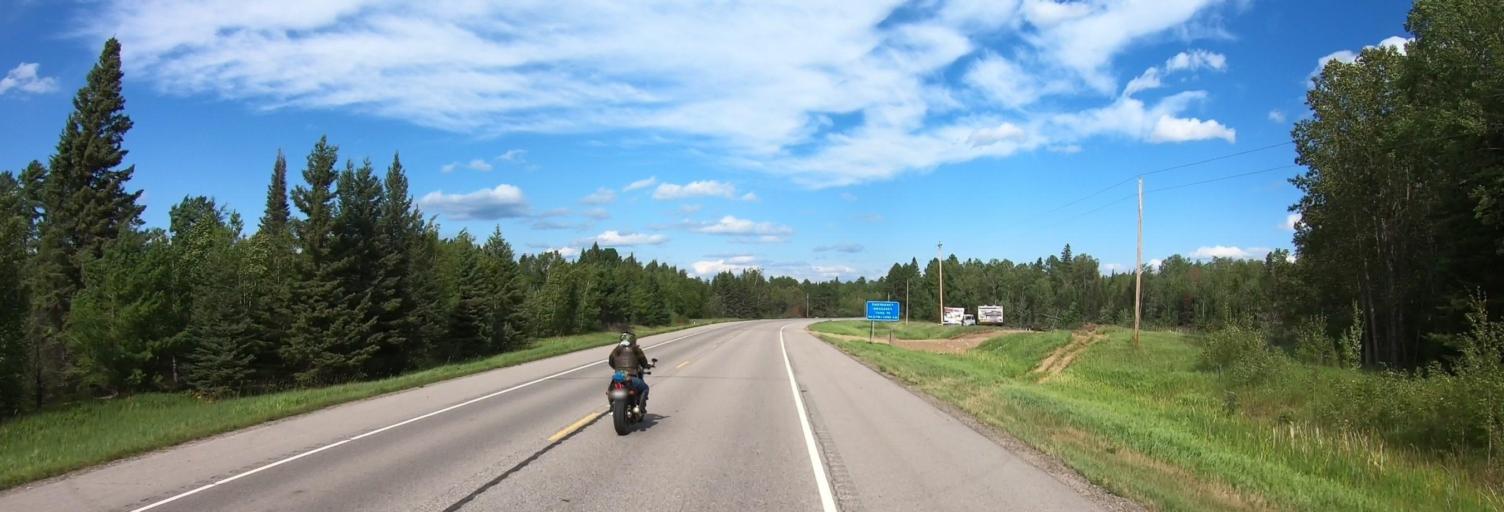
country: US
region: Minnesota
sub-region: Saint Louis County
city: Ely
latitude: 47.8978
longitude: -91.8953
